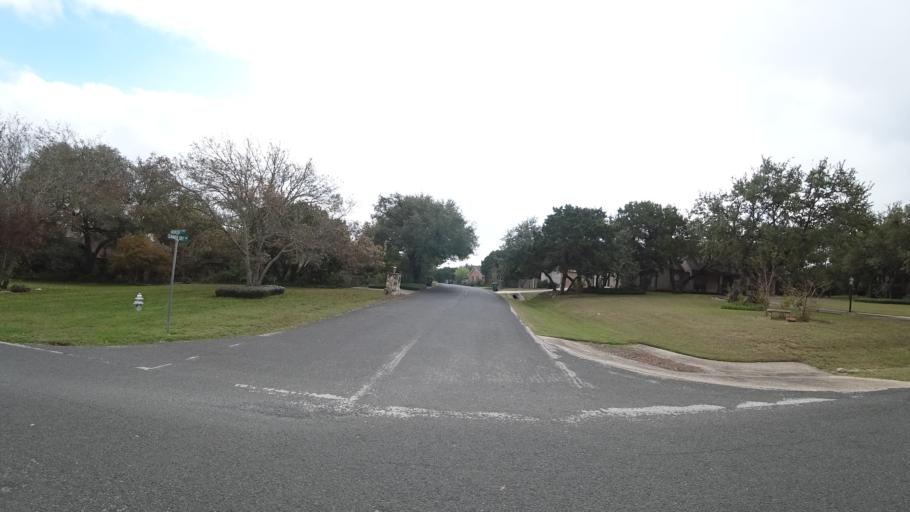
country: US
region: Texas
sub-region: Travis County
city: Barton Creek
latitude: 30.2545
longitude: -97.9076
